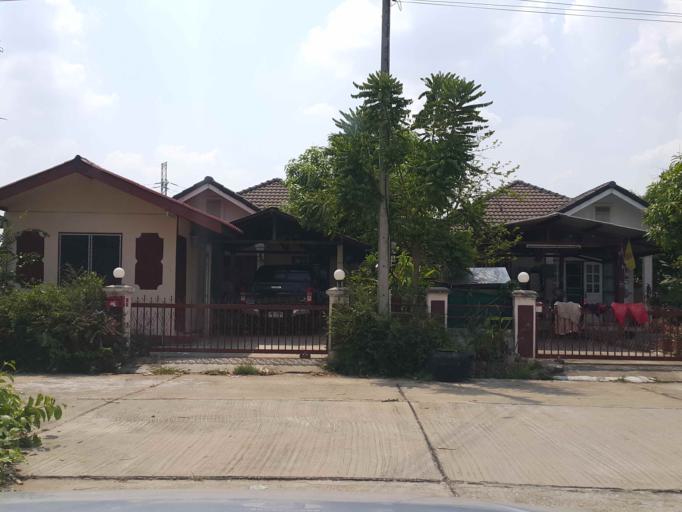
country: TH
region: Chiang Mai
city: Hang Dong
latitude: 18.7088
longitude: 98.9572
